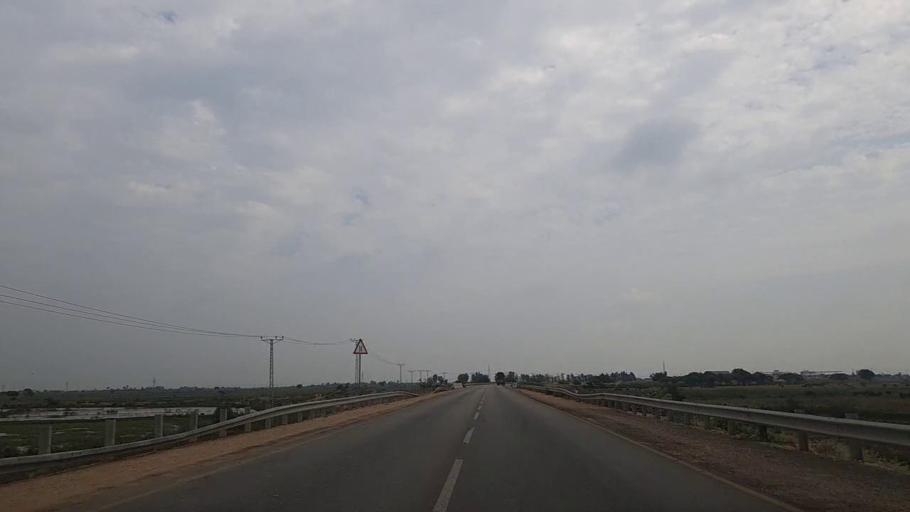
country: PK
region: Sindh
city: Daro Mehar
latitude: 24.6183
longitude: 68.0815
